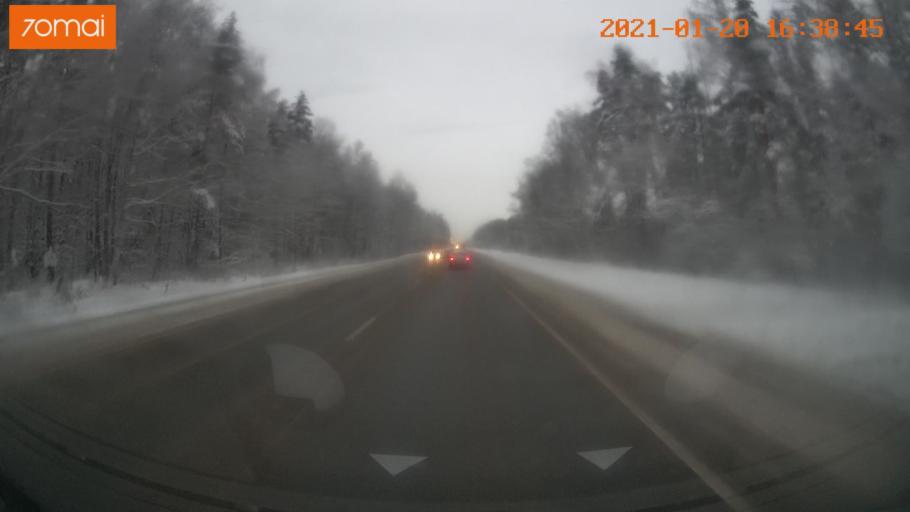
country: RU
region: Vladimir
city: Orgtrud
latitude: 56.2068
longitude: 40.6964
